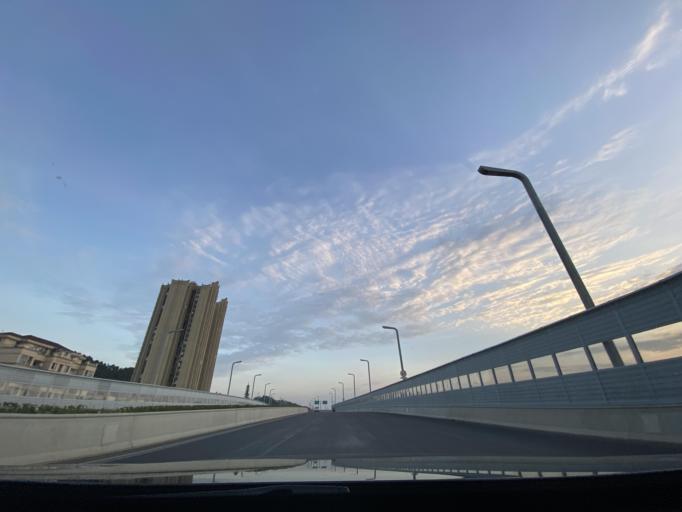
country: CN
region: Sichuan
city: Longquan
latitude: 30.5994
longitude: 104.3081
